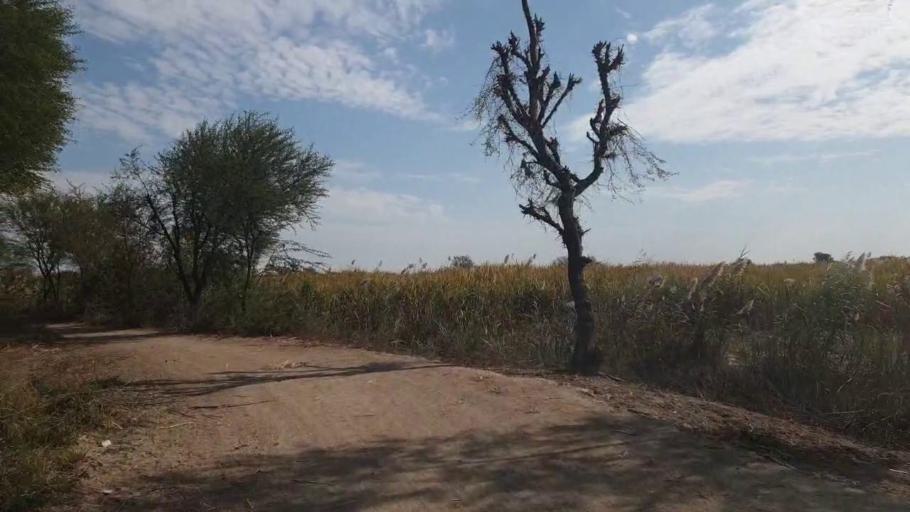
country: PK
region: Sindh
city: Jhol
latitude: 26.0102
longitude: 68.8767
